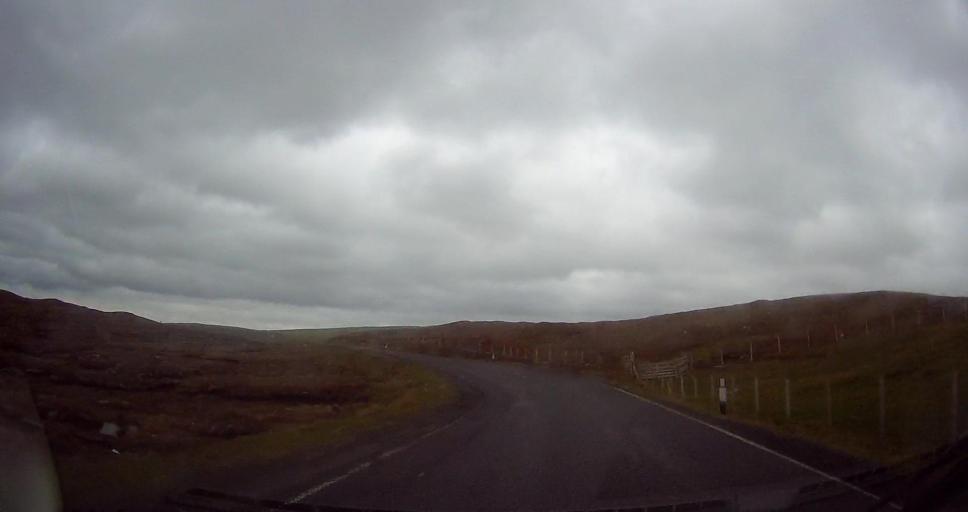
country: GB
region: Scotland
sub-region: Shetland Islands
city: Lerwick
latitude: 60.4800
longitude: -1.4189
